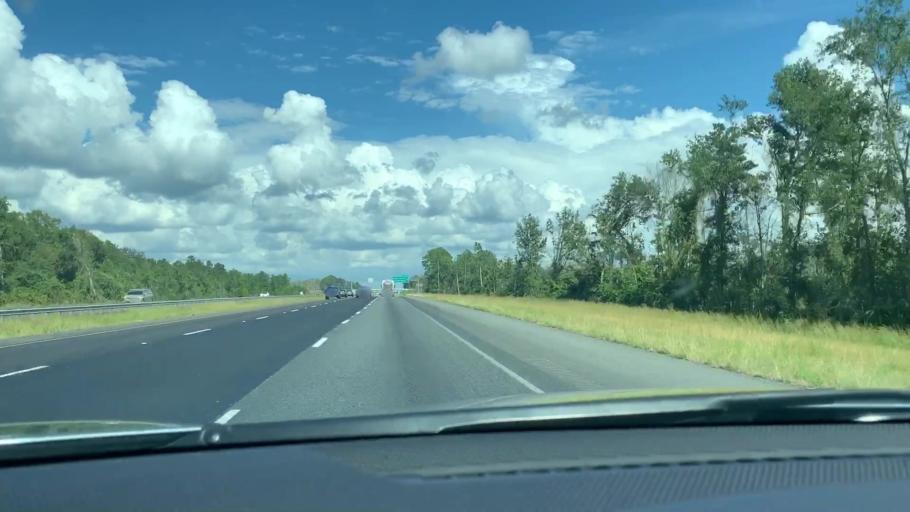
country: US
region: Georgia
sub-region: Camden County
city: Woodbine
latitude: 31.0491
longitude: -81.6468
